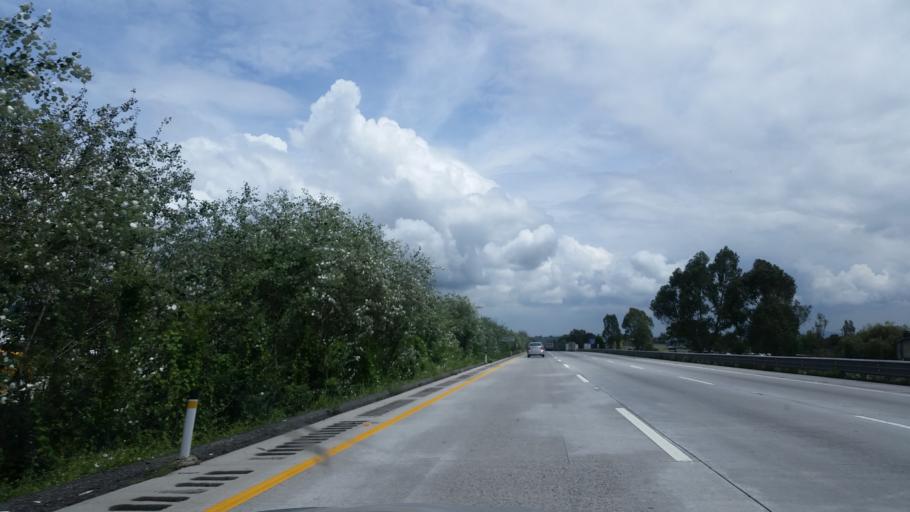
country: MX
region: Mexico
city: San Francisco Soyaniquilpan
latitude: 19.9935
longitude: -99.4736
